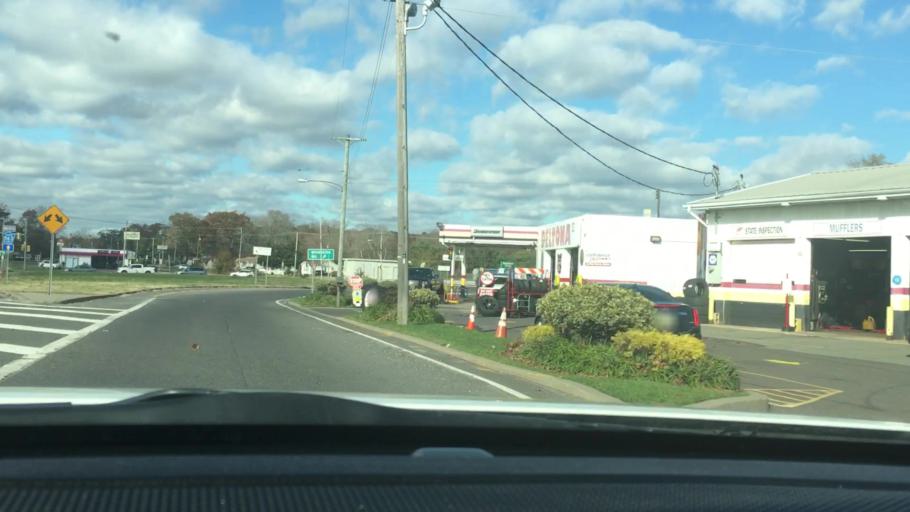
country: US
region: New Jersey
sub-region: Atlantic County
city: Northfield
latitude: 39.4062
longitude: -74.5634
